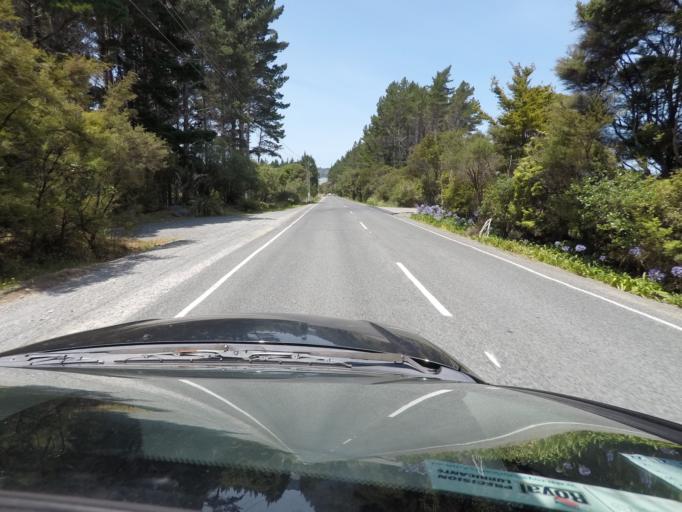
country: NZ
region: Auckland
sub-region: Auckland
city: Warkworth
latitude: -36.3168
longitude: 174.7478
